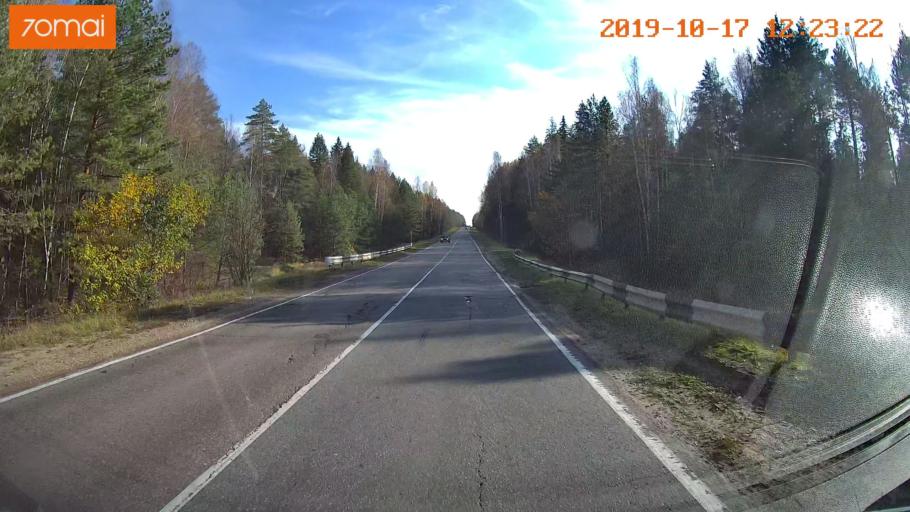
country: RU
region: Rjazan
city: Gus'-Zheleznyy
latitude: 55.0446
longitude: 41.1920
